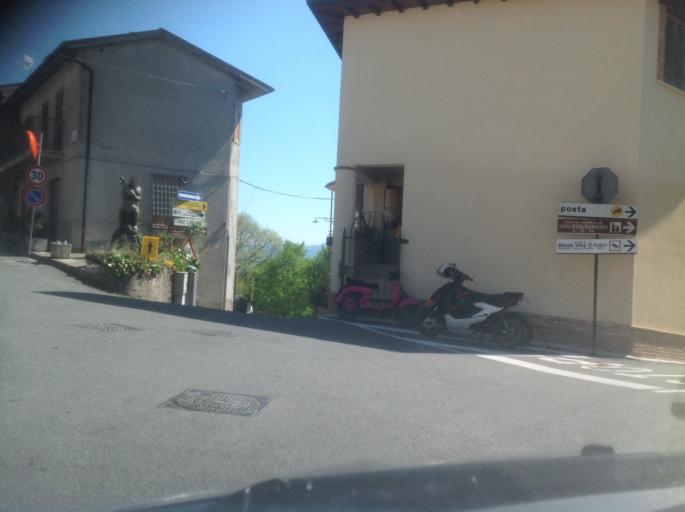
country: IT
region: Latium
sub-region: Provincia di Rieti
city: Colli sul Velino
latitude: 42.4990
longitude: 12.7792
